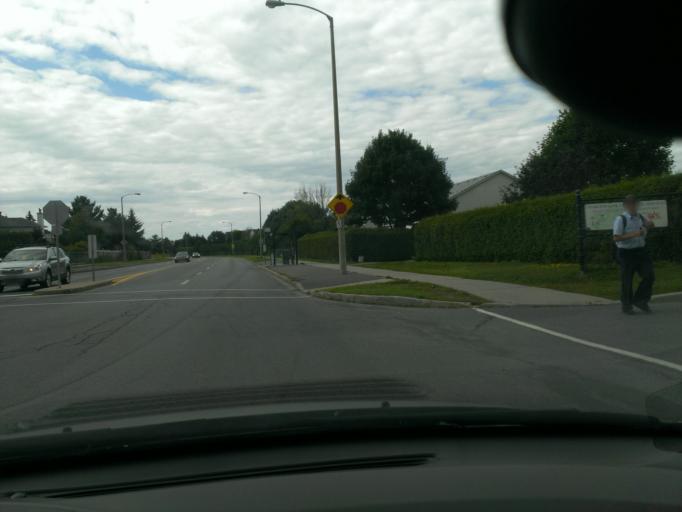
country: CA
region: Ontario
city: Clarence-Rockland
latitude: 45.4755
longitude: -75.4782
